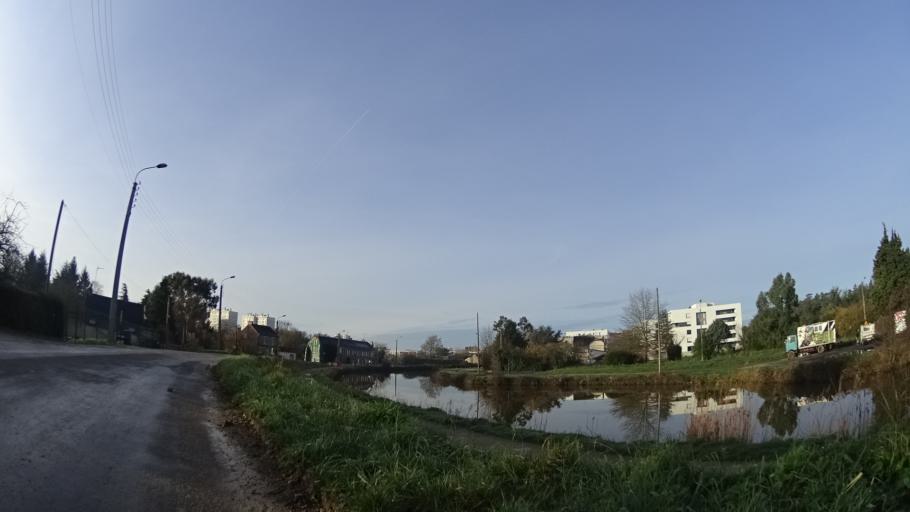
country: FR
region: Brittany
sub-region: Departement d'Ille-et-Vilaine
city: Rennes
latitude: 48.1245
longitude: -1.6746
